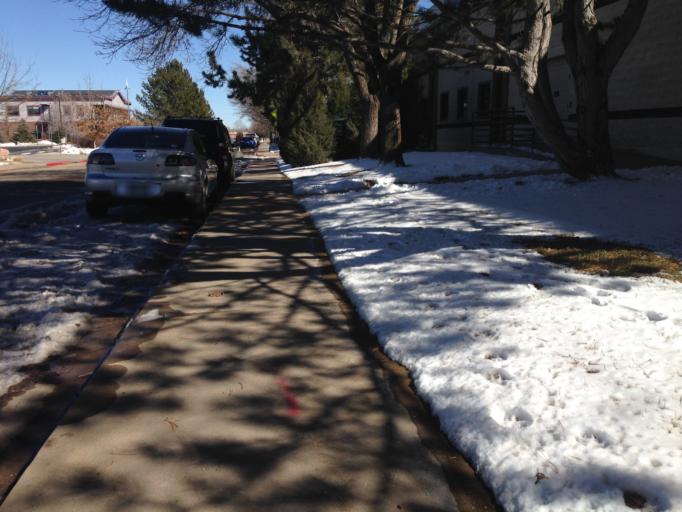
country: US
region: Colorado
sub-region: Boulder County
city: Lafayette
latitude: 39.9892
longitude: -105.0931
